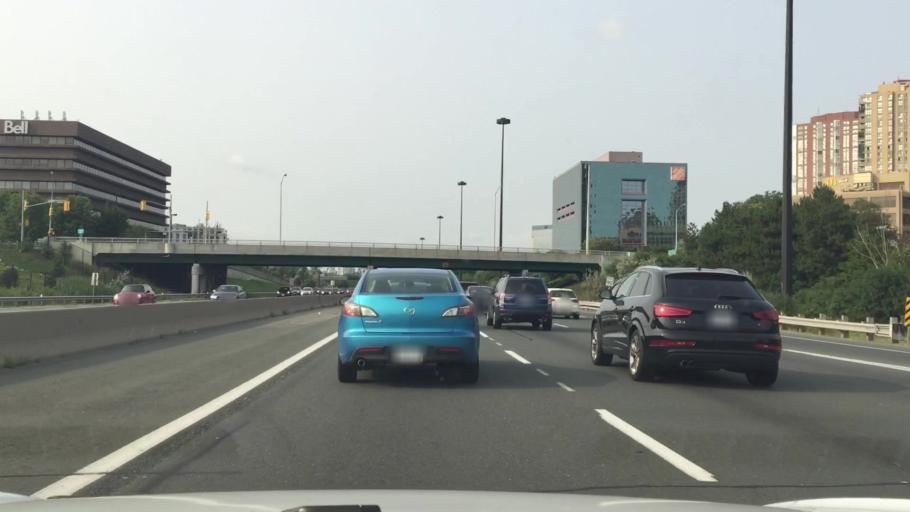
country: CA
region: Ontario
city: Willowdale
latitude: 43.7256
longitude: -79.3303
